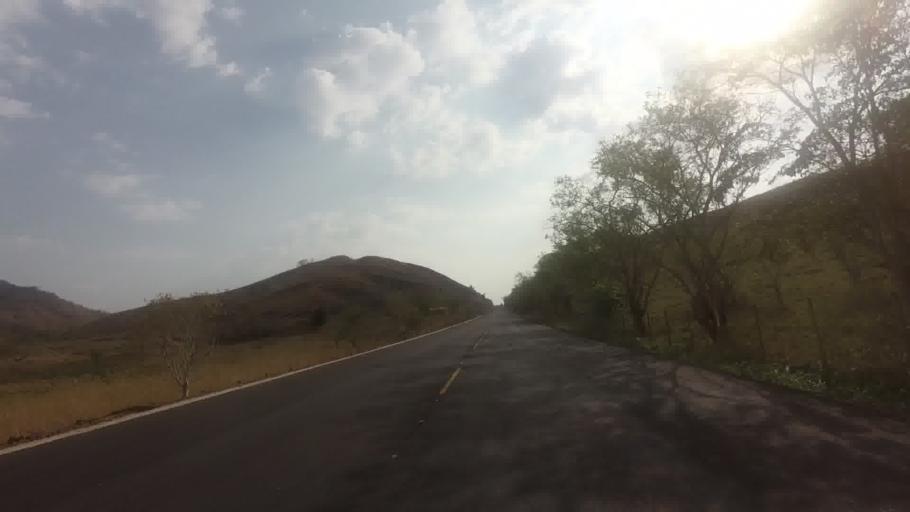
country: BR
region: Rio de Janeiro
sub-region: Itaperuna
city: Itaperuna
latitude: -21.2936
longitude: -41.8259
